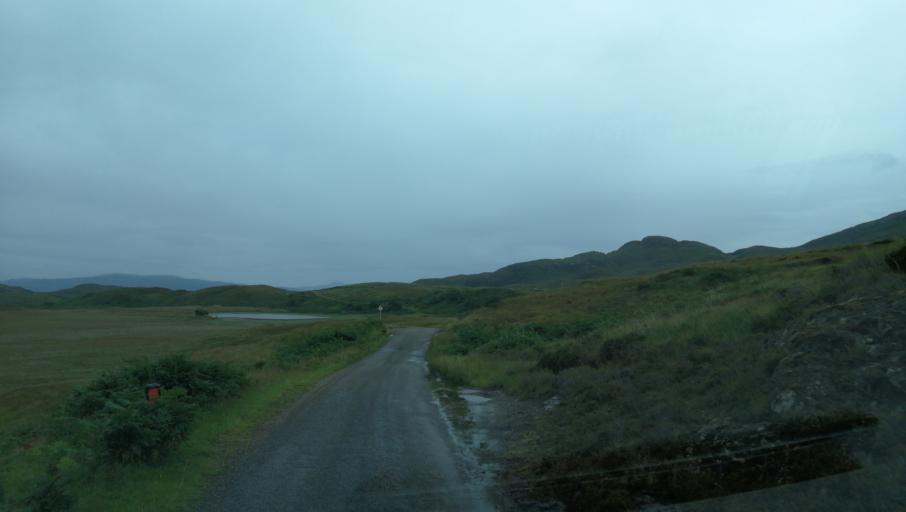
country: GB
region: Scotland
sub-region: Argyll and Bute
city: Isle Of Mull
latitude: 56.7169
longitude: -6.1502
